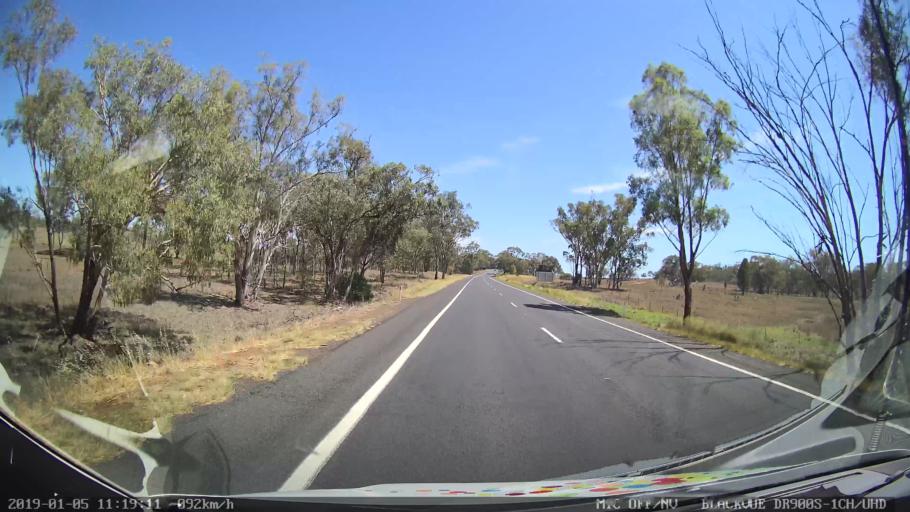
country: AU
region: New South Wales
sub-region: Warrumbungle Shire
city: Coonabarabran
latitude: -31.3070
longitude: 149.2969
